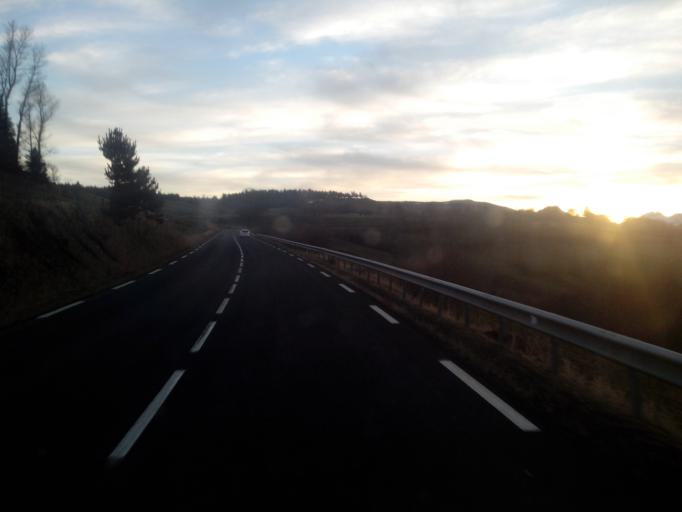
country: FR
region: Auvergne
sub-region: Departement du Cantal
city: Murat
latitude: 45.1580
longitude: 2.8259
